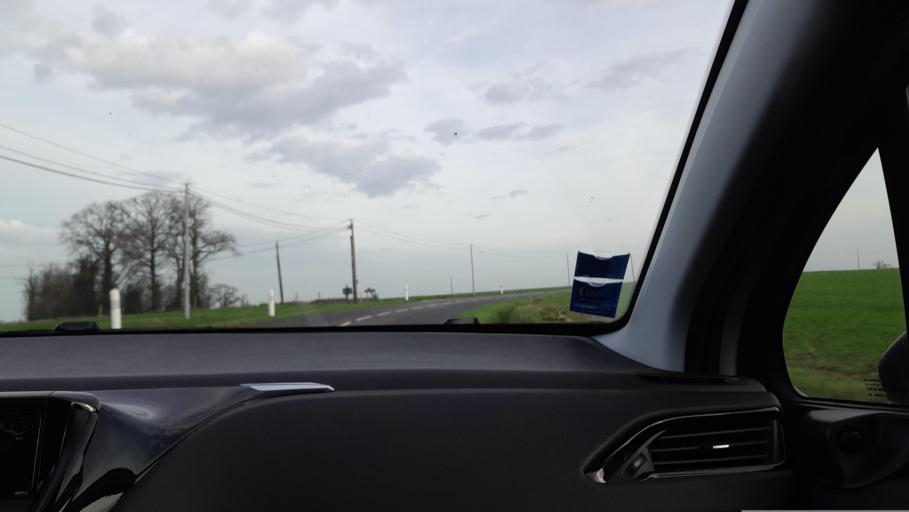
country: FR
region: Brittany
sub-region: Departement d'Ille-et-Vilaine
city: La Guerche-de-Bretagne
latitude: 47.9567
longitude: -1.1708
